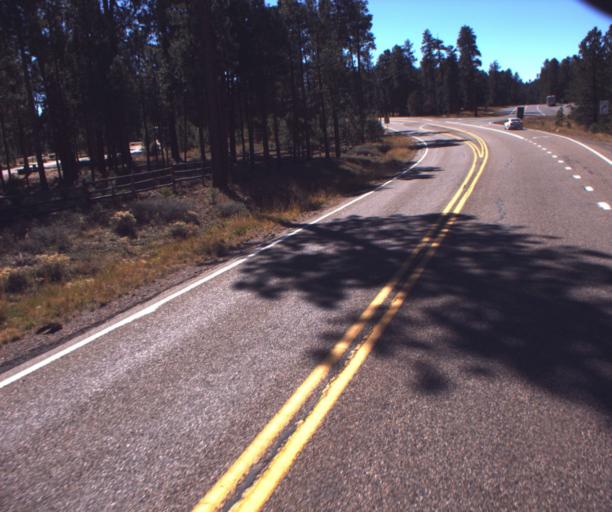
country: US
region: Arizona
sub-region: Coconino County
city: Fredonia
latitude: 36.7159
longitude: -112.2157
